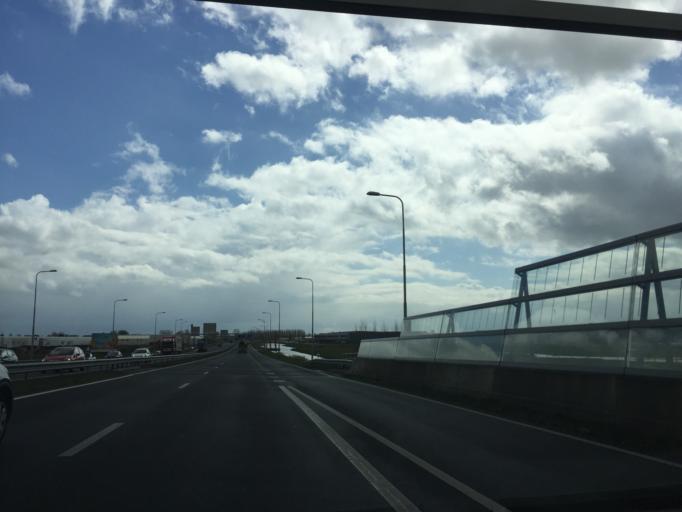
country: NL
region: North Holland
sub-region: Gemeente Aalsmeer
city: Aalsmeer
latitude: 52.2685
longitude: 4.7889
